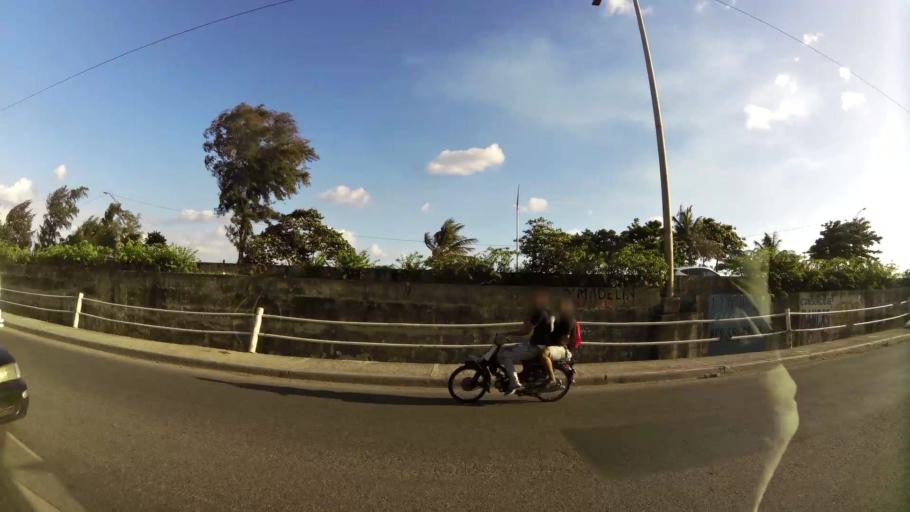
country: DO
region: Santo Domingo
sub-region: Santo Domingo
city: Santo Domingo Este
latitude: 18.4664
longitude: -69.7955
